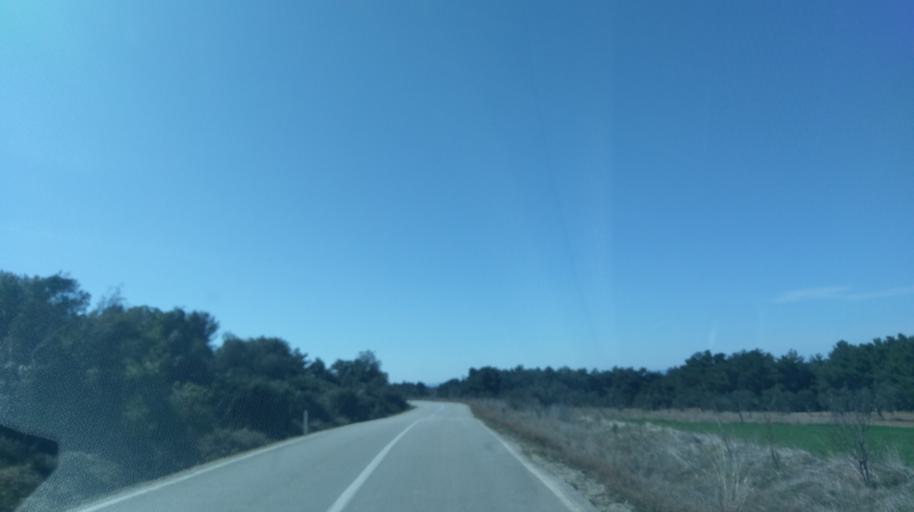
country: TR
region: Canakkale
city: Intepe
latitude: 40.1049
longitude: 26.2335
